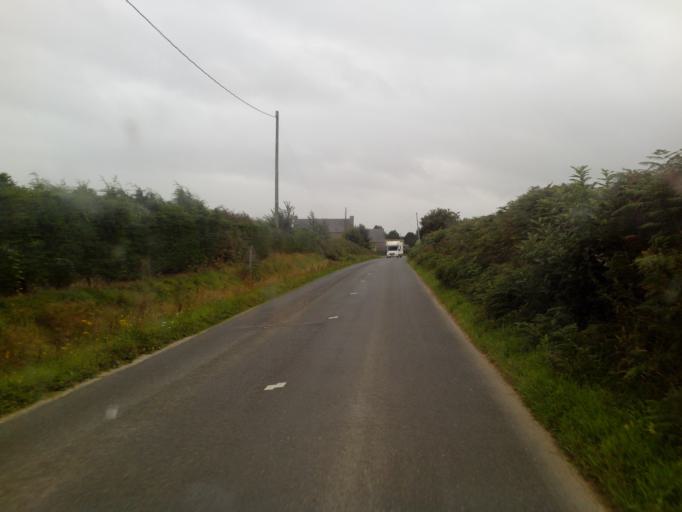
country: FR
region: Brittany
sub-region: Departement des Cotes-d'Armor
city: Lezardrieux
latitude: 48.8135
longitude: -3.1019
